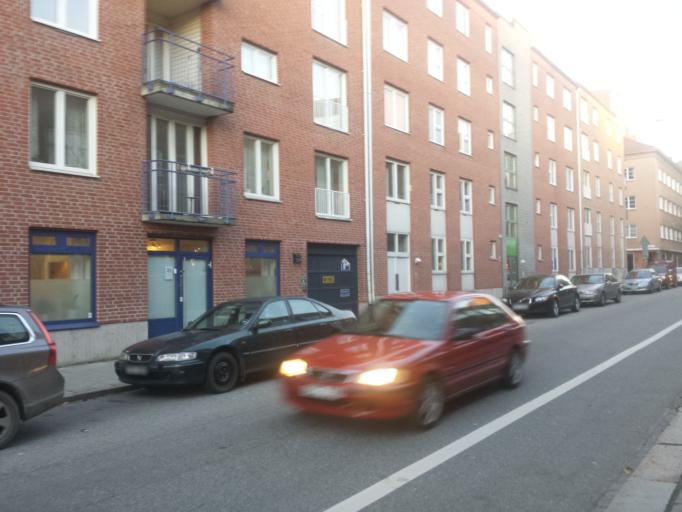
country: SE
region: Skane
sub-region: Malmo
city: Malmoe
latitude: 55.6052
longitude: 13.0101
